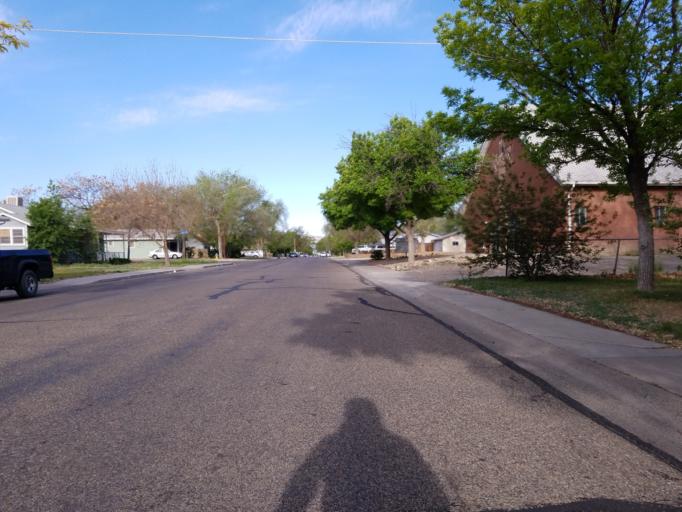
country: US
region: Colorado
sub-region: Mesa County
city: Grand Junction
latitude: 39.0810
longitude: -108.5446
